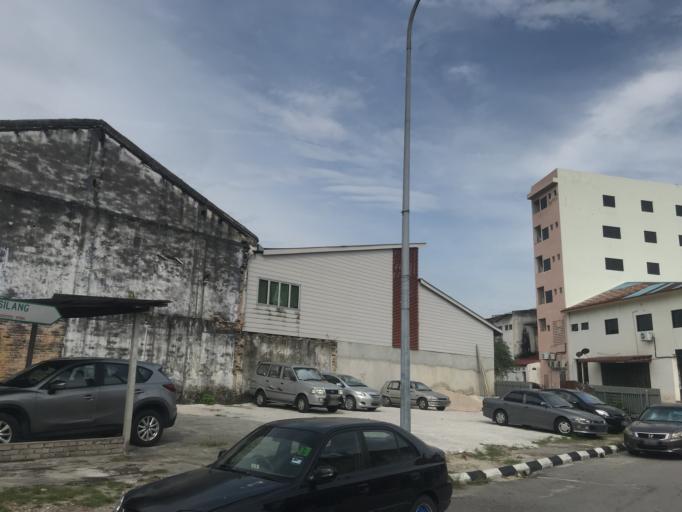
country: MY
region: Perak
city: Ipoh
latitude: 4.5925
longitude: 101.0761
